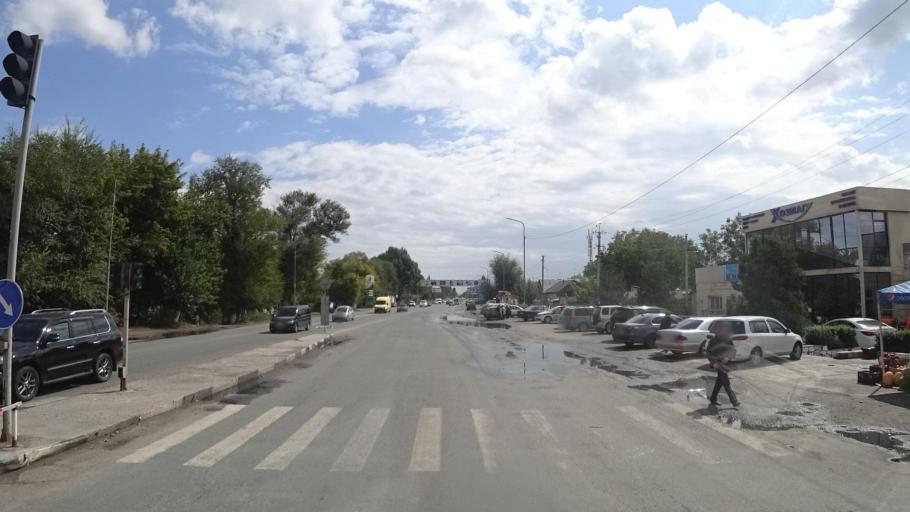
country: KG
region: Chuy
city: Lebedinovka
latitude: 42.8856
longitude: 74.6791
